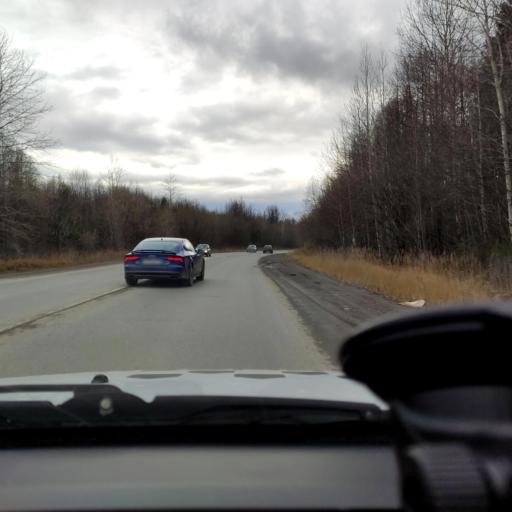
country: RU
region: Perm
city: Ferma
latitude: 57.9600
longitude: 56.3434
